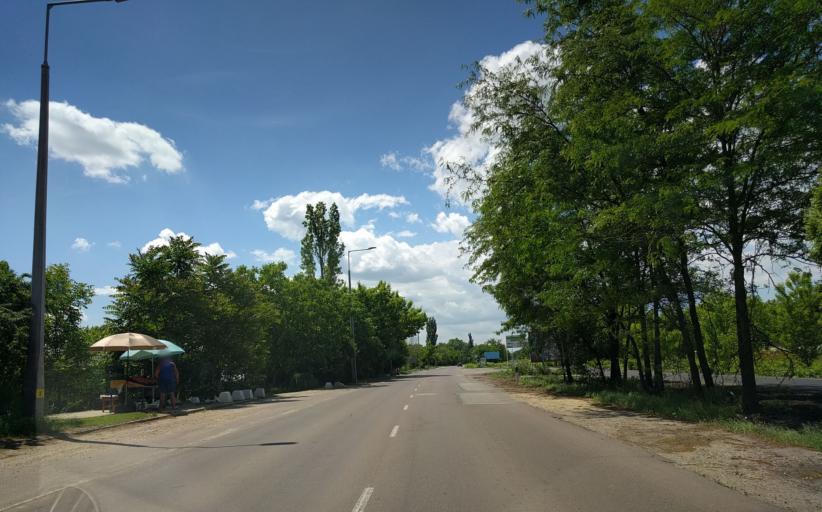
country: HU
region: Jasz-Nagykun-Szolnok
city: Toszeg
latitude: 47.1405
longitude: 20.1568
